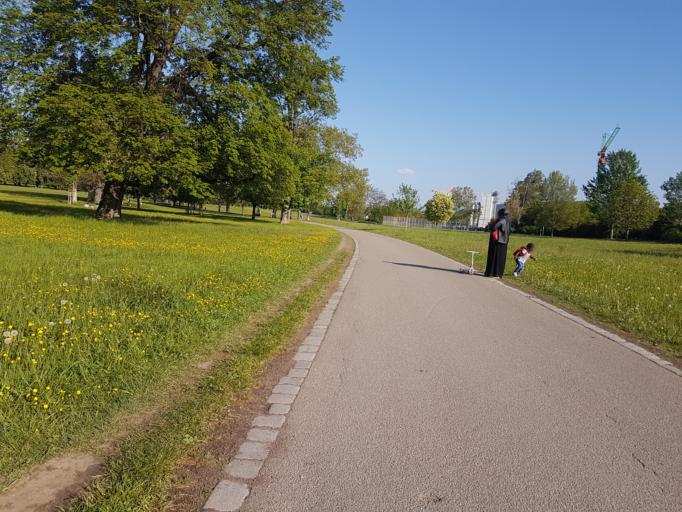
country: DE
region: Baden-Wuerttemberg
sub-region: Regierungsbezirk Stuttgart
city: Stuttgart-Ost
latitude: 48.8038
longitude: 9.1932
